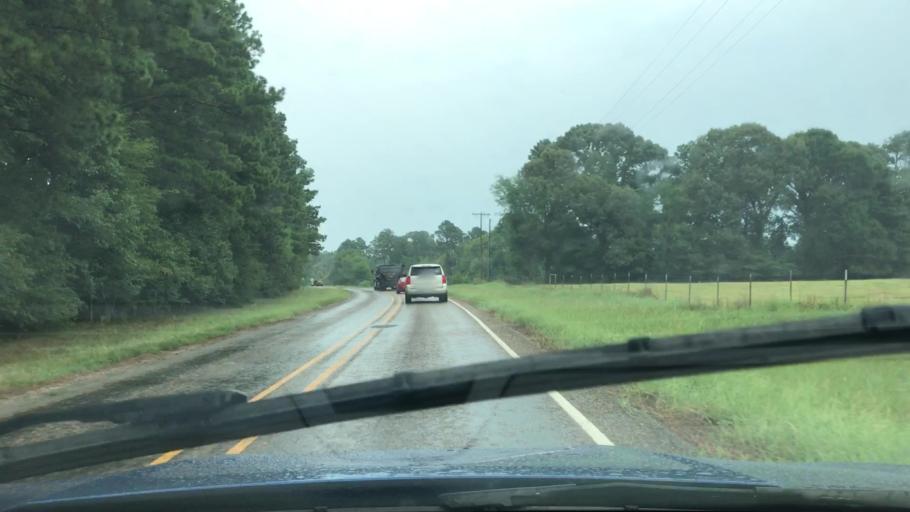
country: US
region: Texas
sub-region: Harrison County
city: Waskom
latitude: 32.4835
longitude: -94.1154
